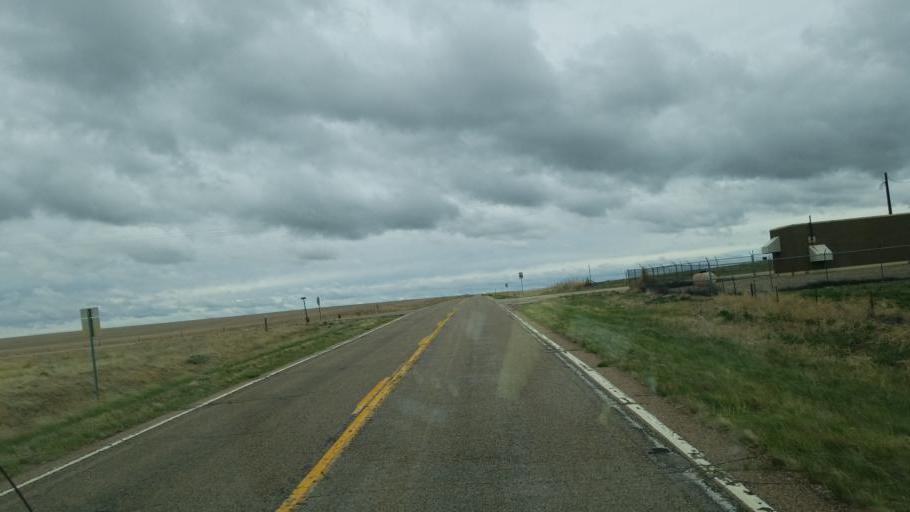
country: US
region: Colorado
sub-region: Lincoln County
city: Hugo
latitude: 38.8512
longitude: -103.6253
